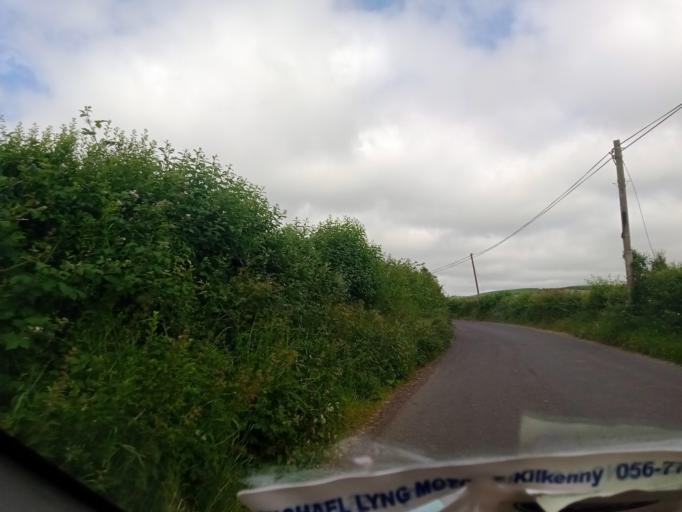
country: IE
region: Leinster
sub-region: Kilkenny
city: Ballyragget
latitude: 52.7633
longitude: -7.4597
